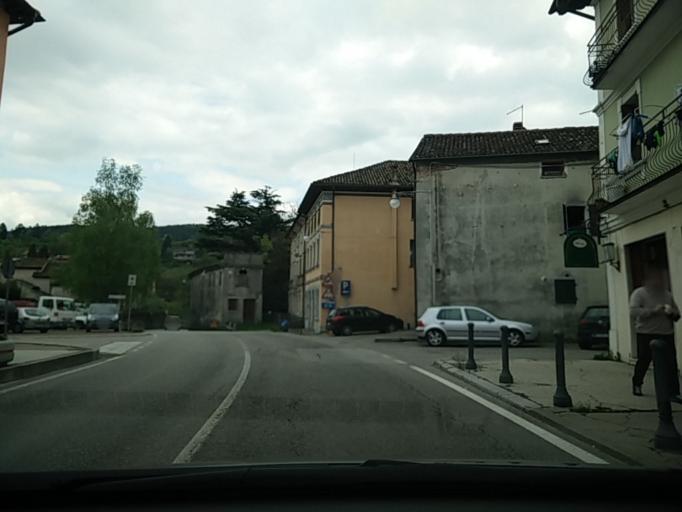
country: IT
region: Veneto
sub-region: Provincia di Belluno
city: Ponte nell'Alpi
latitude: 46.1741
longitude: 12.2836
